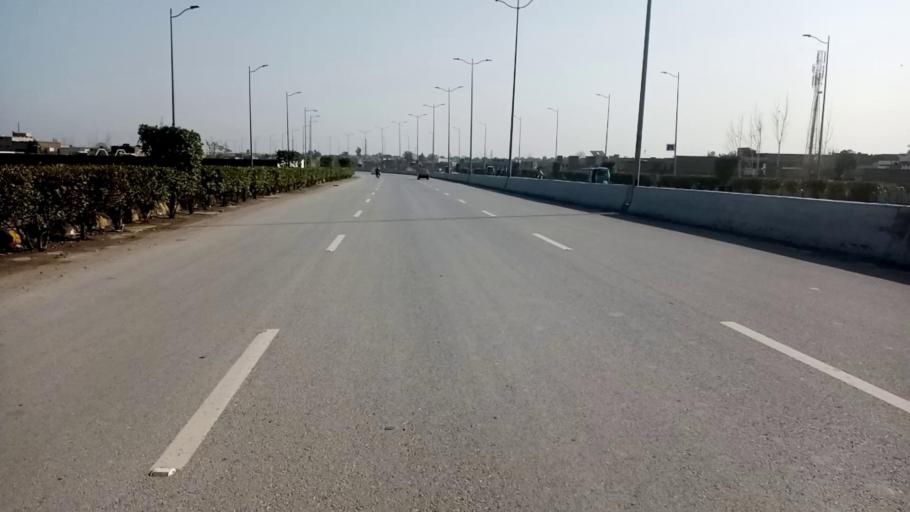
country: PK
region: Khyber Pakhtunkhwa
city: Peshawar
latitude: 34.0325
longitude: 71.5426
